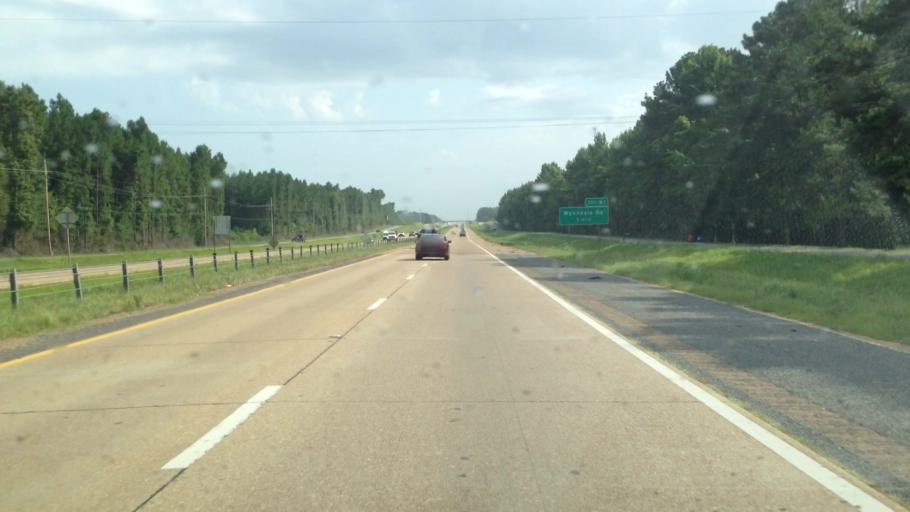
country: US
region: Mississippi
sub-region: Hinds County
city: Terry
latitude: 32.1159
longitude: -90.2951
